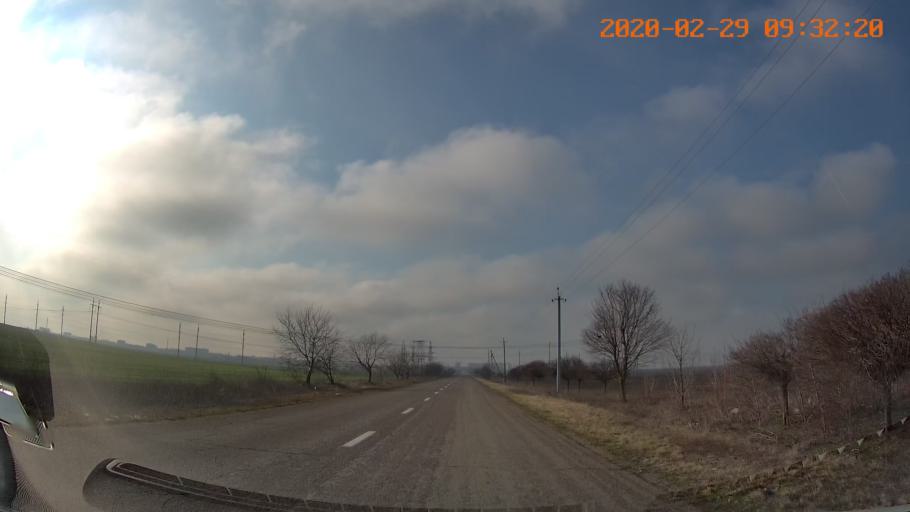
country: MD
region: Telenesti
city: Dnestrovsc
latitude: 46.6409
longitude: 29.9066
